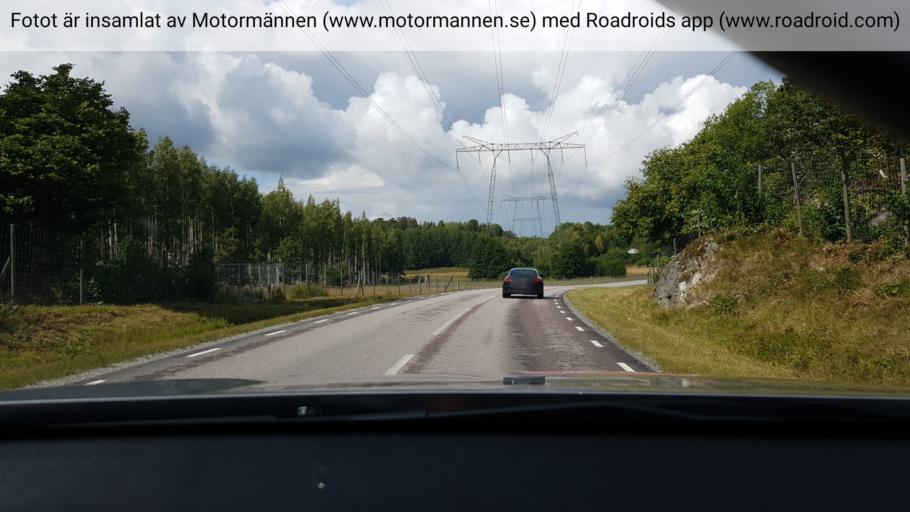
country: SE
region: Stockholm
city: Stenhamra
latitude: 59.3493
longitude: 17.6249
